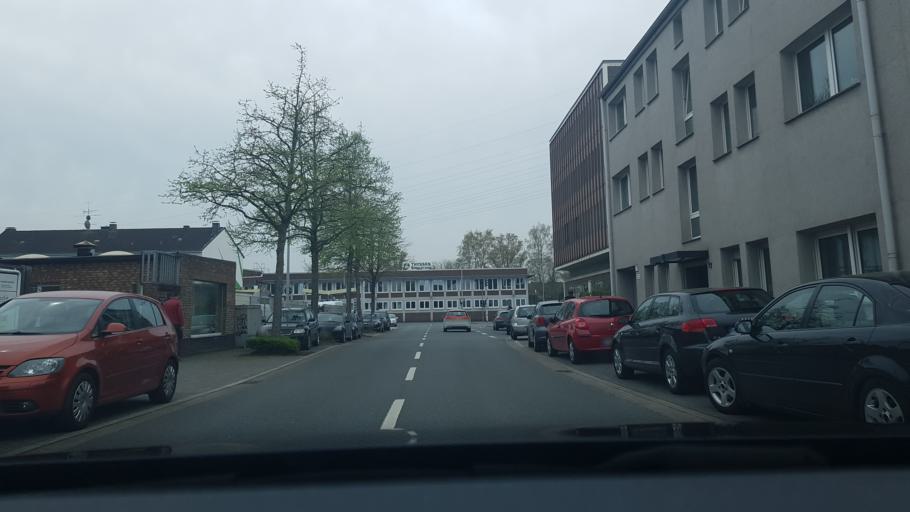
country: DE
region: North Rhine-Westphalia
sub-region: Regierungsbezirk Dusseldorf
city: Muelheim (Ruhr)
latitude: 51.4384
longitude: 6.8776
